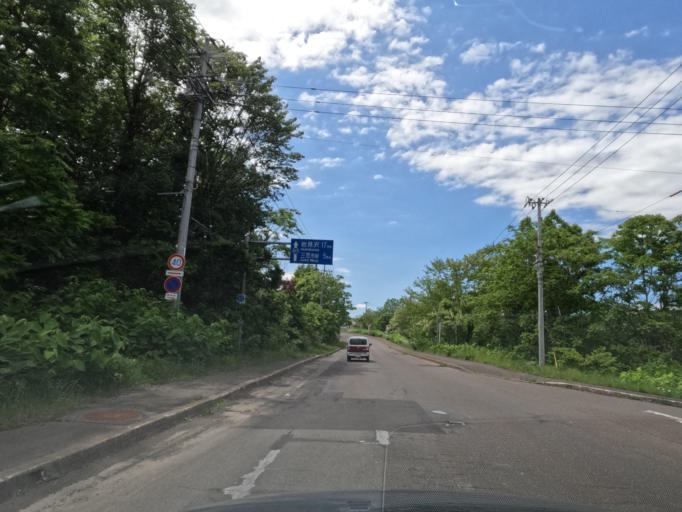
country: JP
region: Hokkaido
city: Bibai
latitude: 43.2535
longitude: 141.9196
